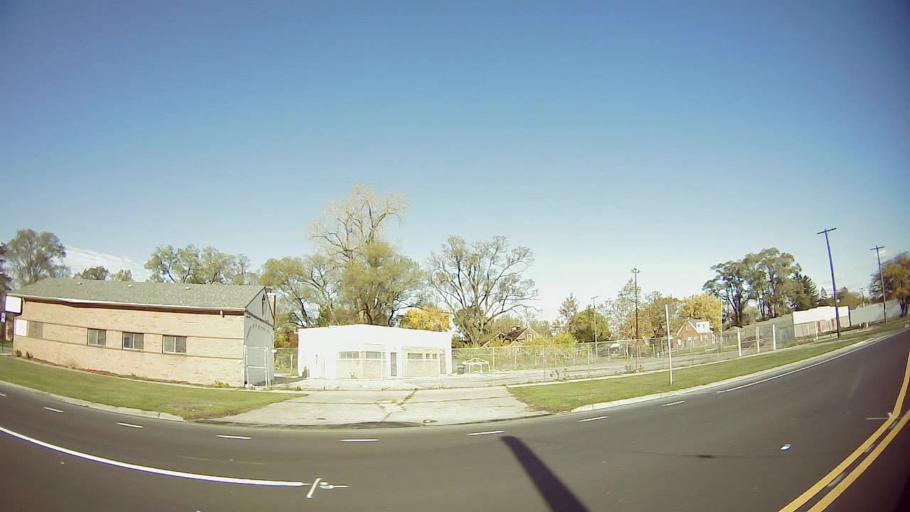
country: US
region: Michigan
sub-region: Wayne County
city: Dearborn
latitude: 42.3590
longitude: -83.1525
